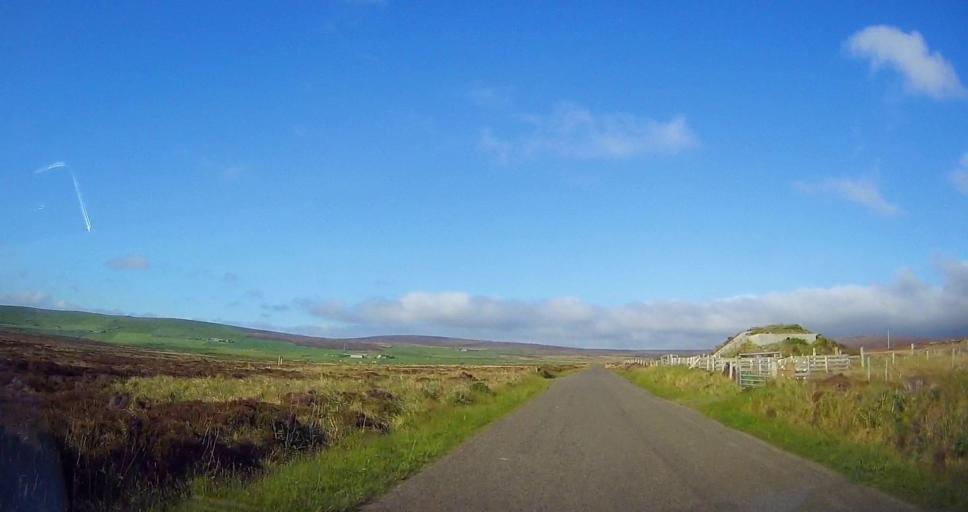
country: GB
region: Scotland
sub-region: Orkney Islands
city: Stromness
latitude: 59.0795
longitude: -3.1982
